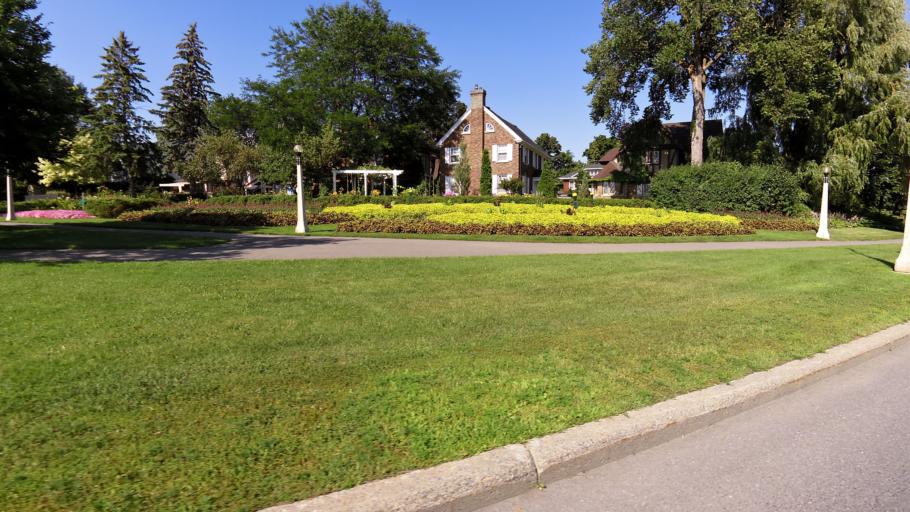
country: CA
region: Ontario
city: Ottawa
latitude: 45.3942
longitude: -75.6977
